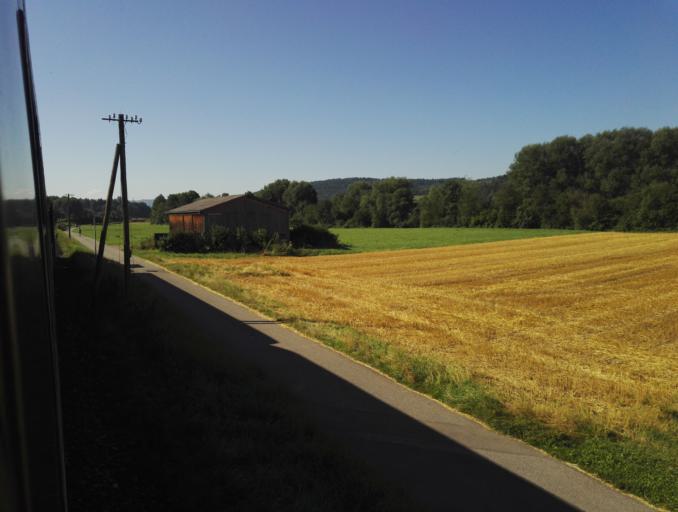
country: DE
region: Baden-Wuerttemberg
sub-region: Regierungsbezirk Stuttgart
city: Rudersberg
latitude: 48.8580
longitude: 9.5375
